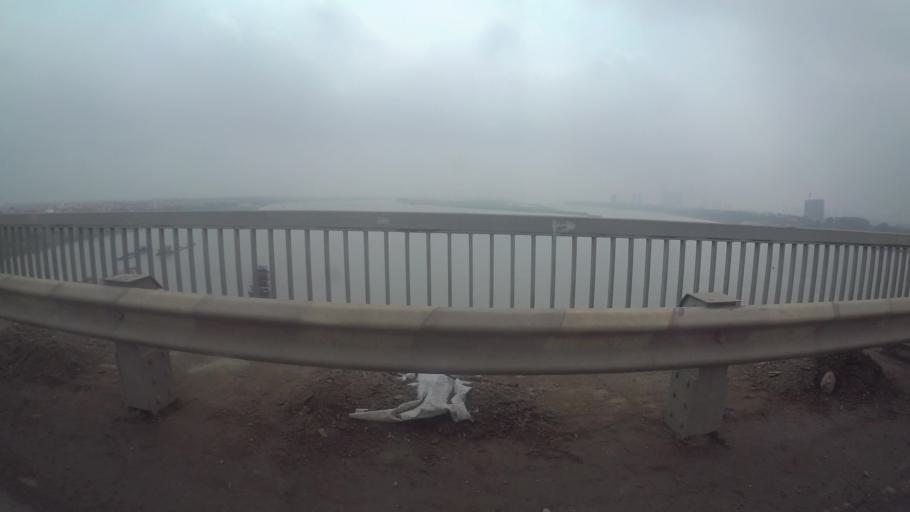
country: VN
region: Ha Noi
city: Tay Ho
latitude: 21.0991
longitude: 105.7866
